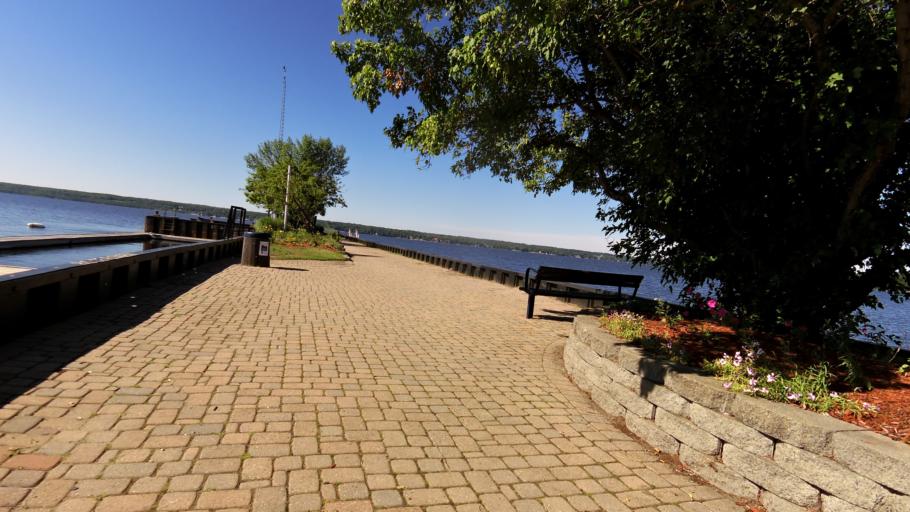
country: CA
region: Quebec
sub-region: Outaouais
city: Shawville
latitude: 45.5166
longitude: -76.4297
